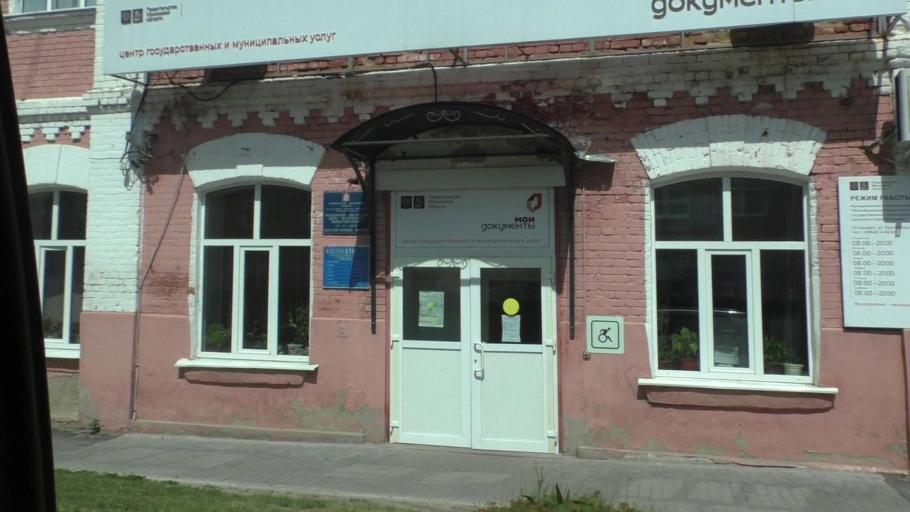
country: RU
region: Moskovskaya
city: Yegor'yevsk
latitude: 55.3842
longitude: 39.0377
